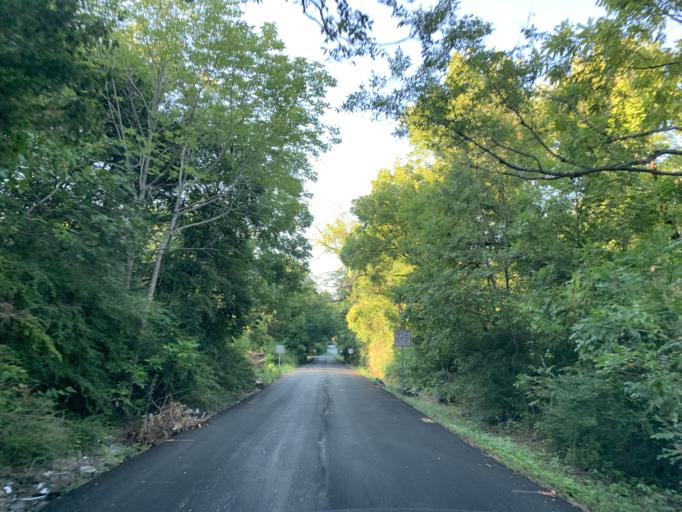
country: US
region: Texas
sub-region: Dallas County
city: Hutchins
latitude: 32.6733
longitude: -96.7822
